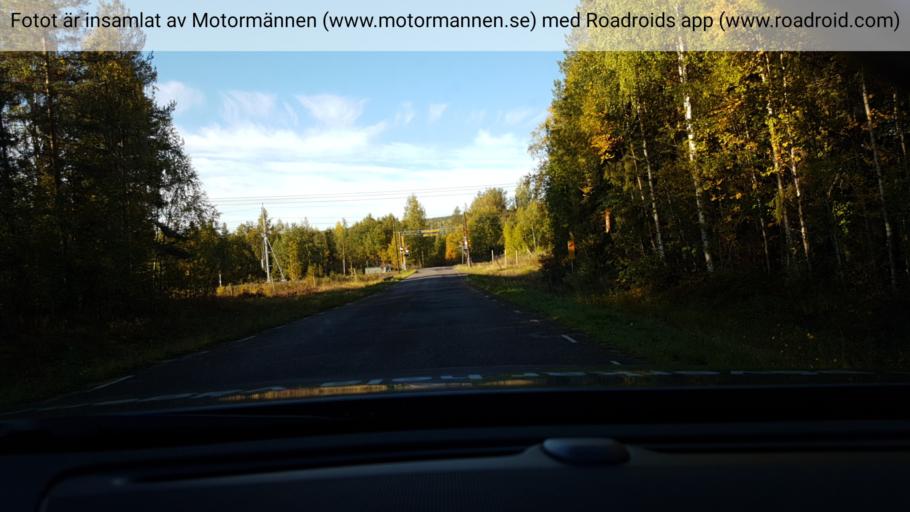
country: SE
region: Norrbotten
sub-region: Bodens Kommun
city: Boden
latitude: 66.0589
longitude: 21.4191
